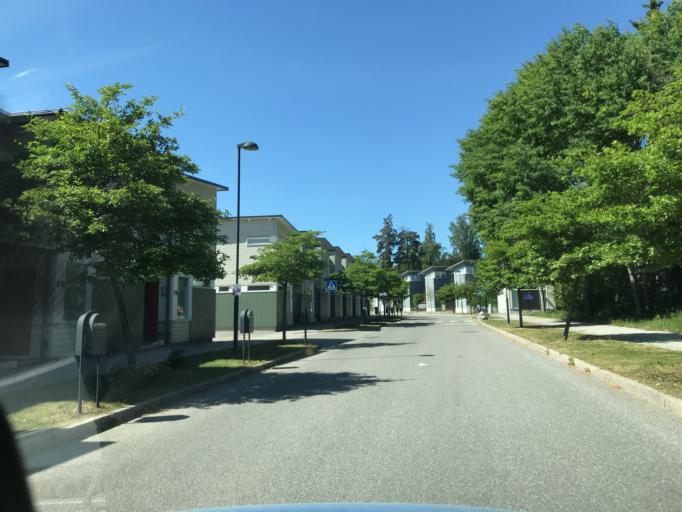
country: SE
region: Stockholm
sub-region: Solna Kommun
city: Rasunda
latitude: 59.4019
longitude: 17.9880
